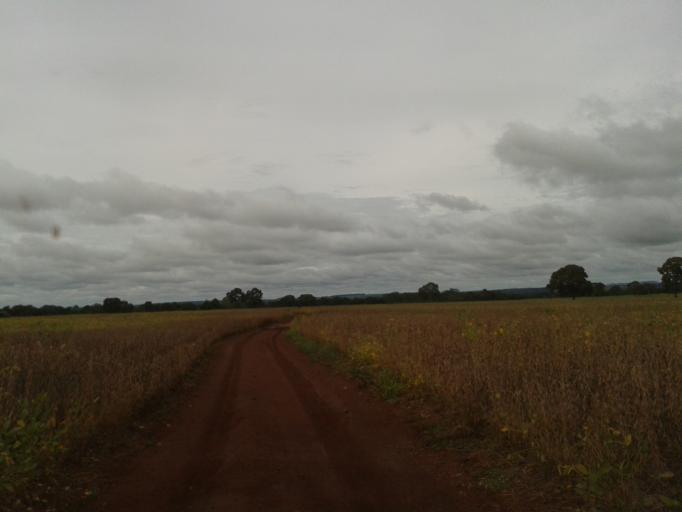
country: BR
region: Minas Gerais
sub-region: Capinopolis
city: Capinopolis
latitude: -18.7764
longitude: -49.7679
